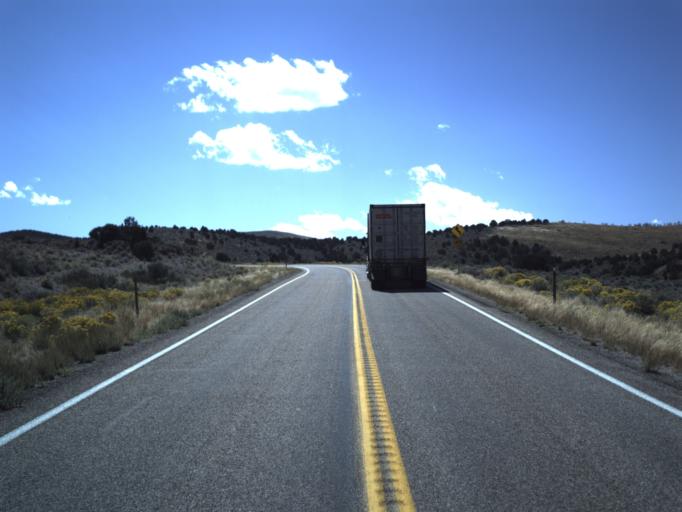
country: US
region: Utah
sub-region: Beaver County
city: Milford
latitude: 38.1159
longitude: -112.9521
